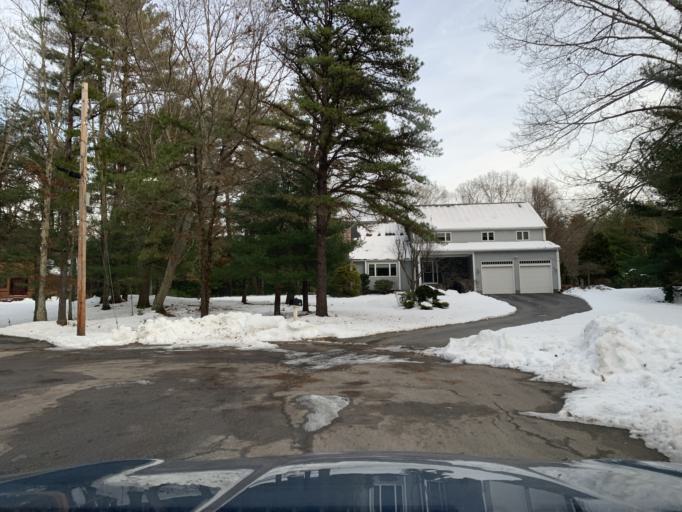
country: US
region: Rhode Island
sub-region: Washington County
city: North Kingstown
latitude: 41.5973
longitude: -71.4485
